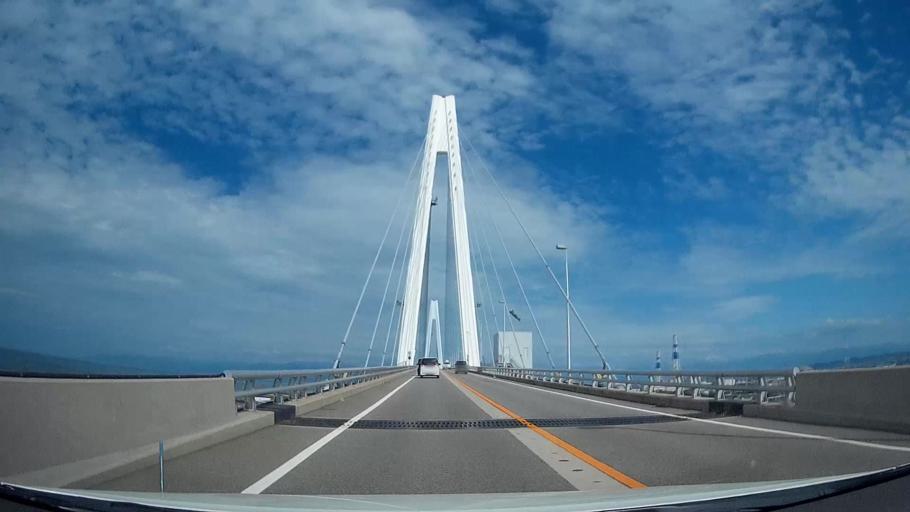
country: JP
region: Toyama
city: Nishishinminato
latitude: 36.7766
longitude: 137.1120
